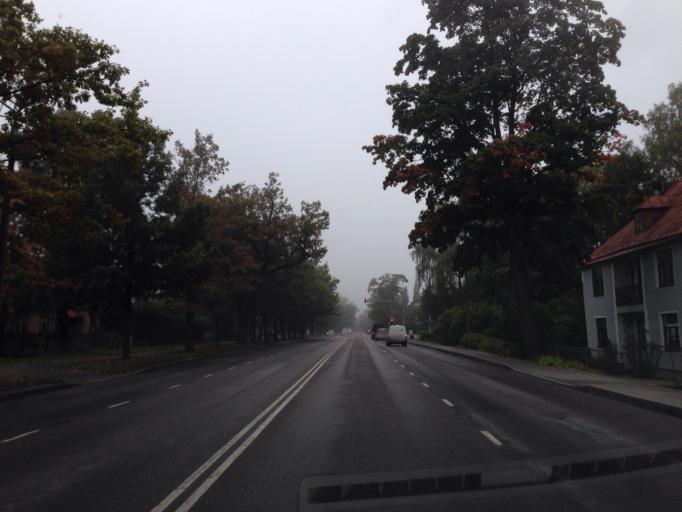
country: EE
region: Tartu
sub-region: Tartu linn
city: Tartu
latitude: 58.3671
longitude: 26.7055
